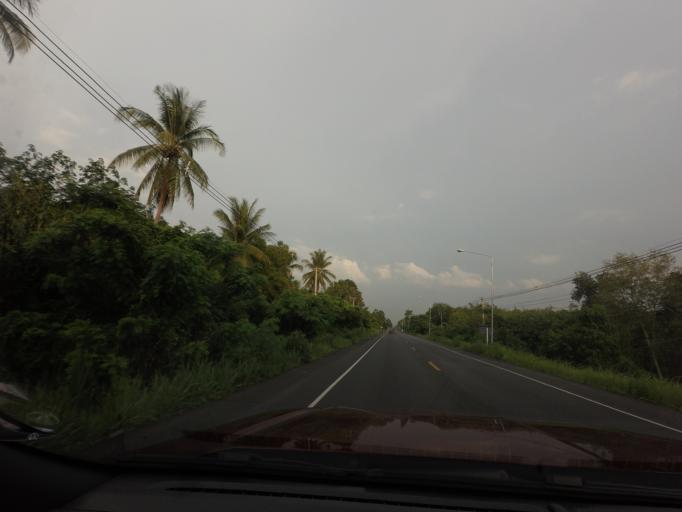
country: TH
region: Pattani
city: Mae Lan
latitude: 6.6606
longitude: 101.1683
